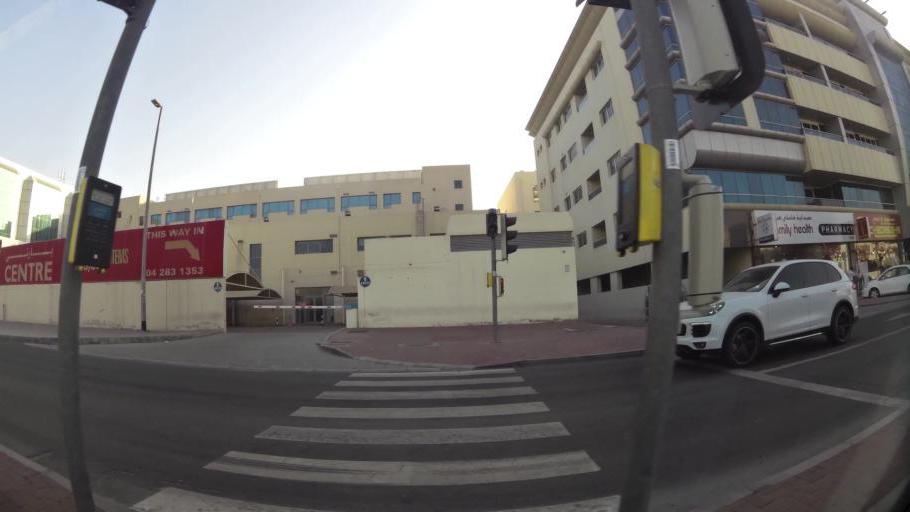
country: AE
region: Ash Shariqah
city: Sharjah
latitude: 25.2475
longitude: 55.3389
